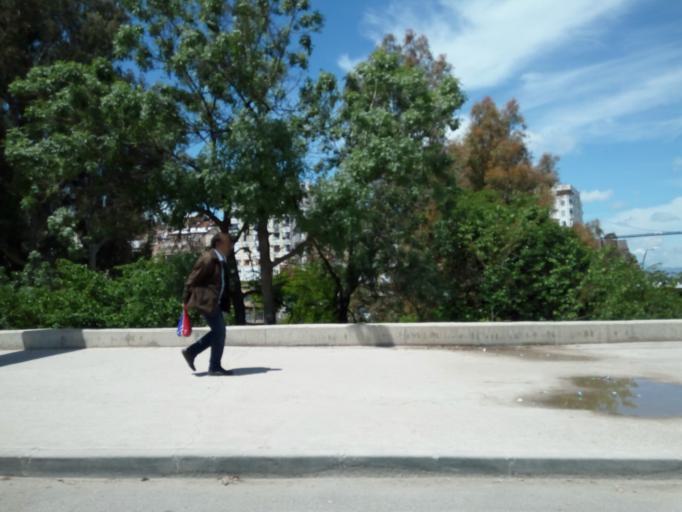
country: DZ
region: Constantine
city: Constantine
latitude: 36.3683
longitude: 6.6187
